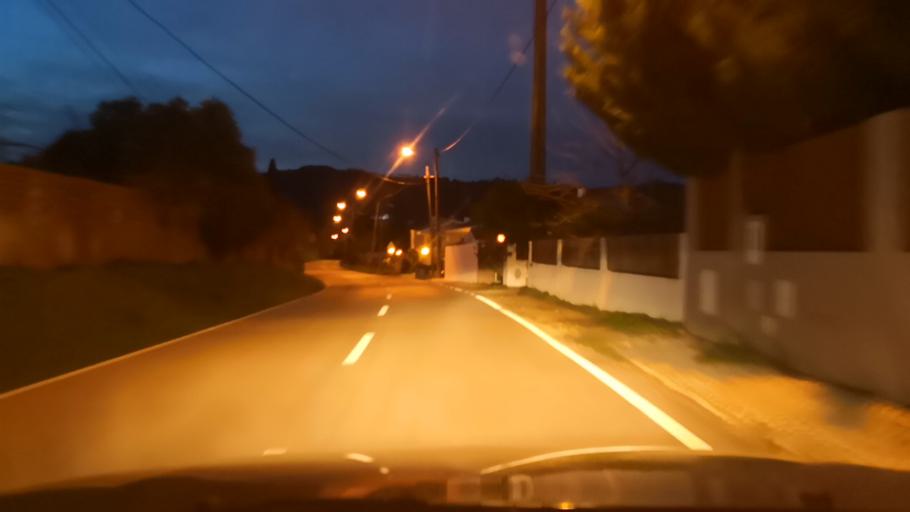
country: PT
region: Setubal
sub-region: Setubal
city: Setubal
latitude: 38.5368
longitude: -8.9012
